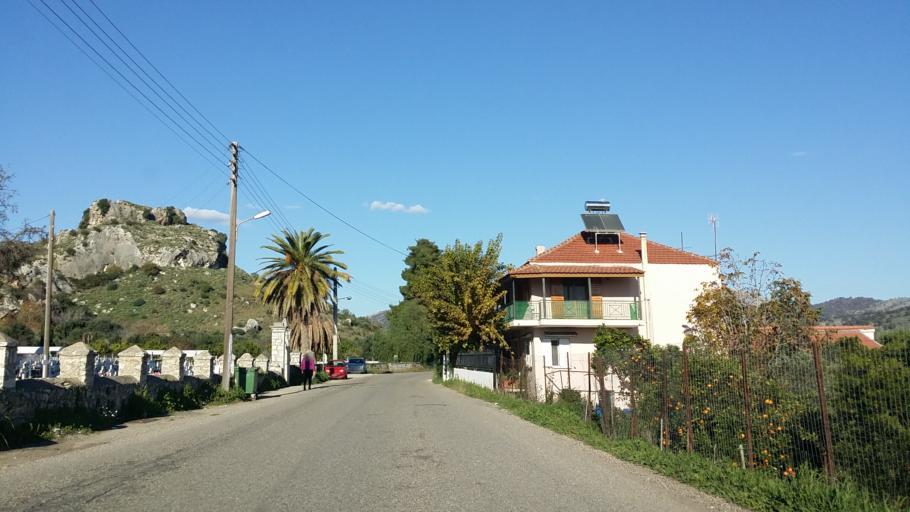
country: GR
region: West Greece
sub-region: Nomos Aitolias kai Akarnanias
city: Astakos
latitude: 38.5428
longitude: 21.0903
